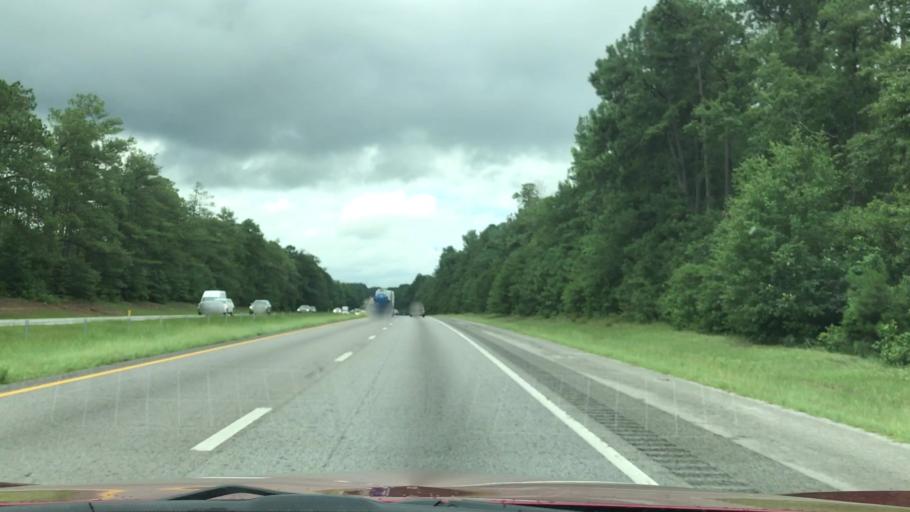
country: US
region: South Carolina
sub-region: Orangeburg County
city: Brookdale
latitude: 33.6023
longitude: -80.8605
